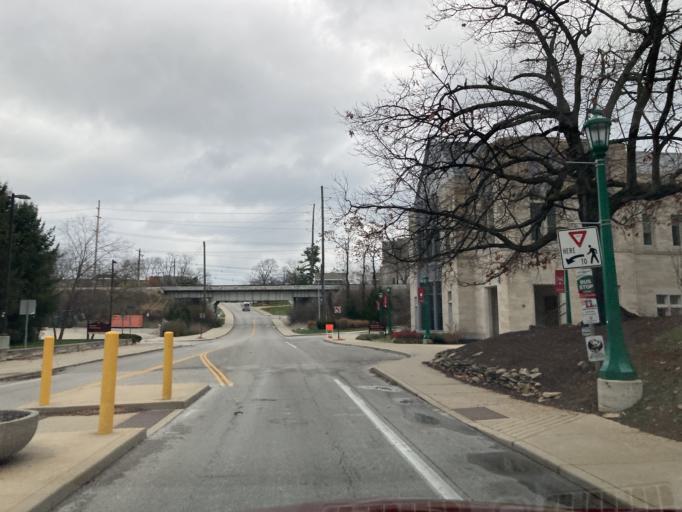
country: US
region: Indiana
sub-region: Monroe County
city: Bloomington
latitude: 39.1727
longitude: -86.5189
